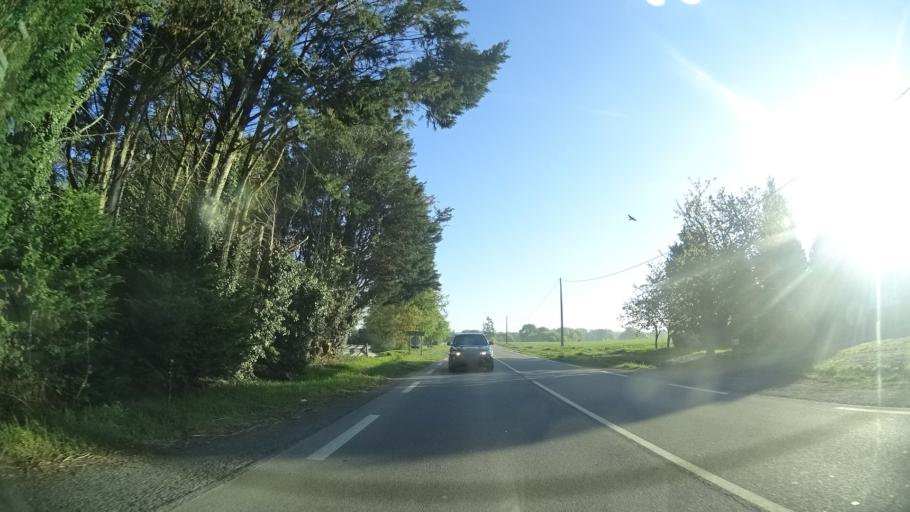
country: FR
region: Brittany
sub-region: Departement d'Ille-et-Vilaine
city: Saint-Just
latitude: 47.7576
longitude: -1.9419
